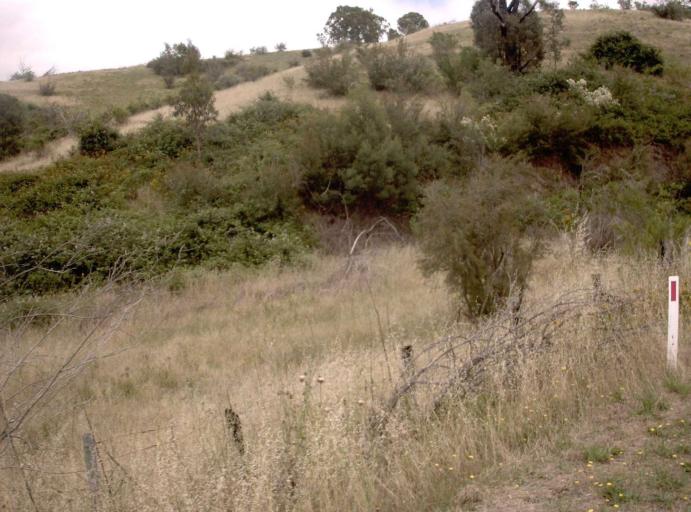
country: AU
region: Victoria
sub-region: Wellington
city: Heyfield
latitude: -37.6957
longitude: 146.6494
